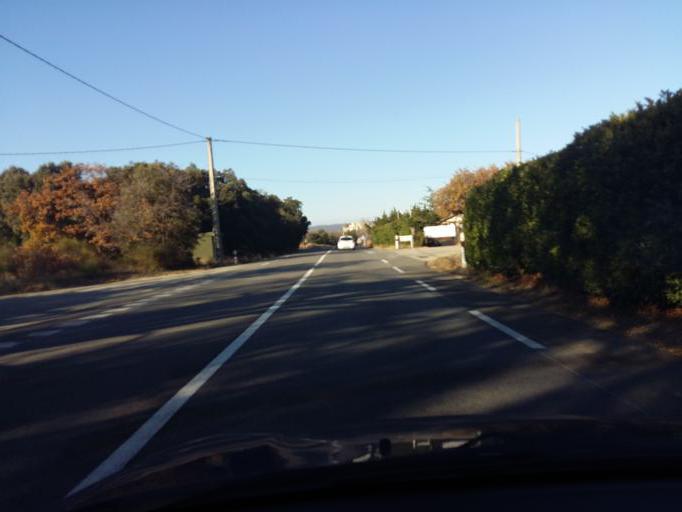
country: FR
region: Rhone-Alpes
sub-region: Departement de la Drome
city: Grignan
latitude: 44.4051
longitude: 4.9155
